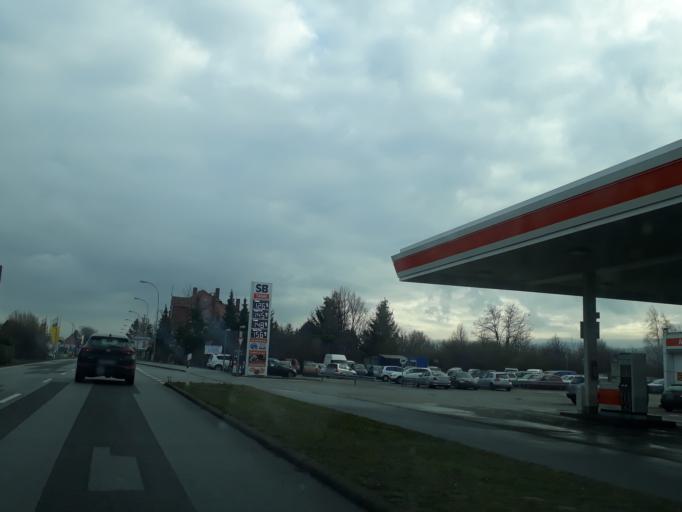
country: DE
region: Saxony
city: Kubschutz
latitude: 51.1734
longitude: 14.4714
